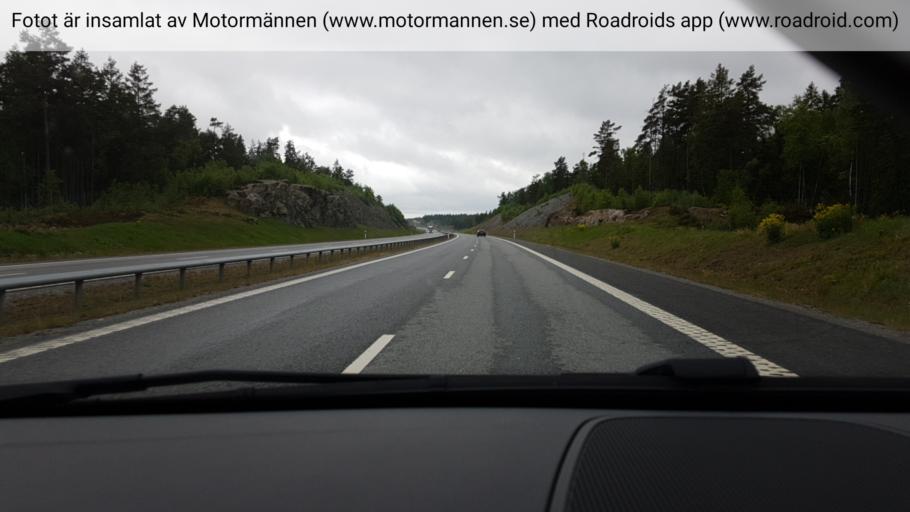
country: SE
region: Stockholm
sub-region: Nynashamns Kommun
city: Osmo
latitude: 59.0445
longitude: 17.9770
